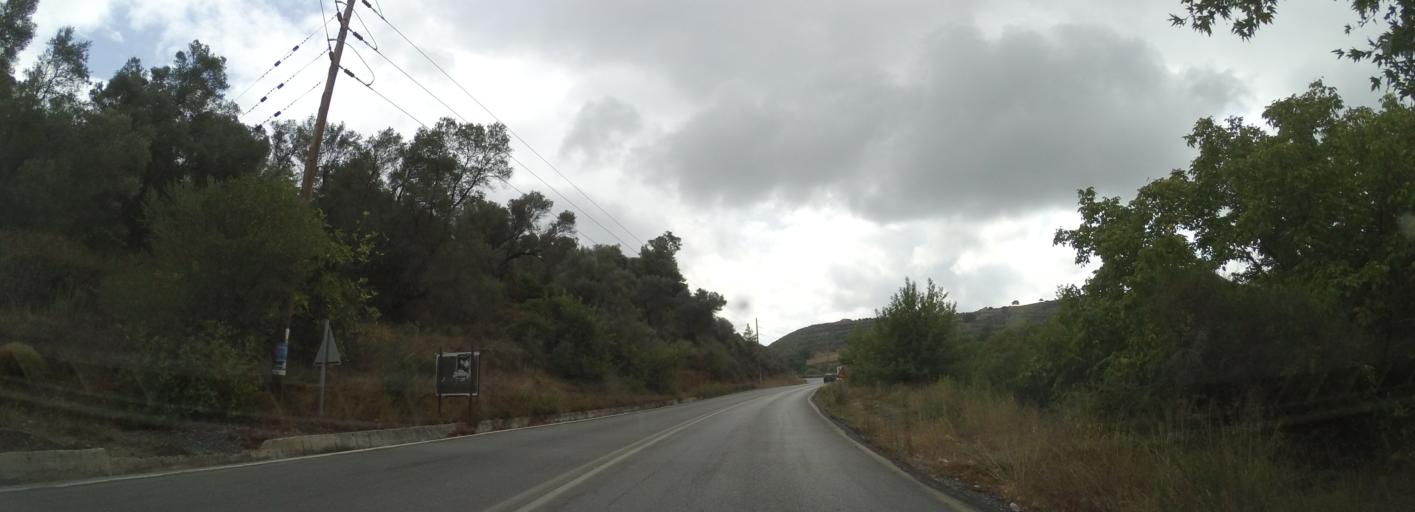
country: GR
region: Crete
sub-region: Nomos Rethymnis
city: Agia Foteini
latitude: 35.2213
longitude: 24.5109
